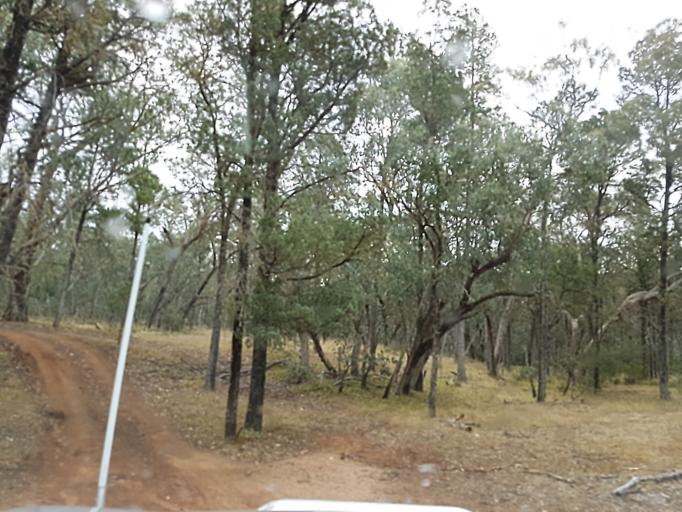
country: AU
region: New South Wales
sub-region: Snowy River
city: Jindabyne
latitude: -36.9440
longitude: 148.3945
